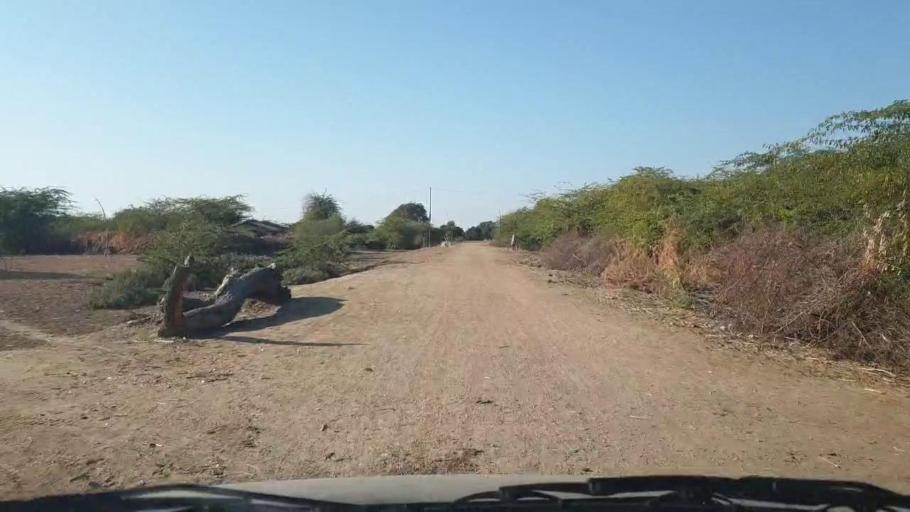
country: PK
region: Sindh
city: Samaro
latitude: 25.3646
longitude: 69.2914
